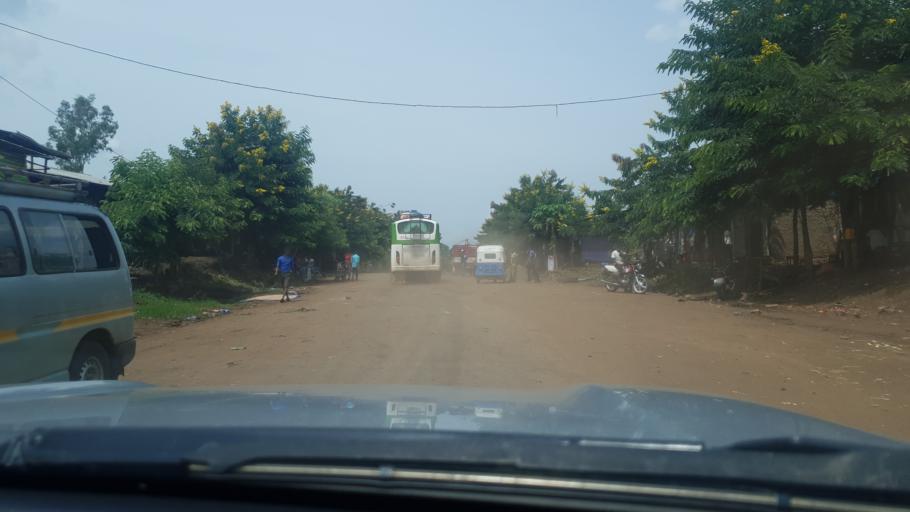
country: ET
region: Southern Nations, Nationalities, and People's Region
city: Mizan Teferi
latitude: 6.7020
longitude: 35.1879
